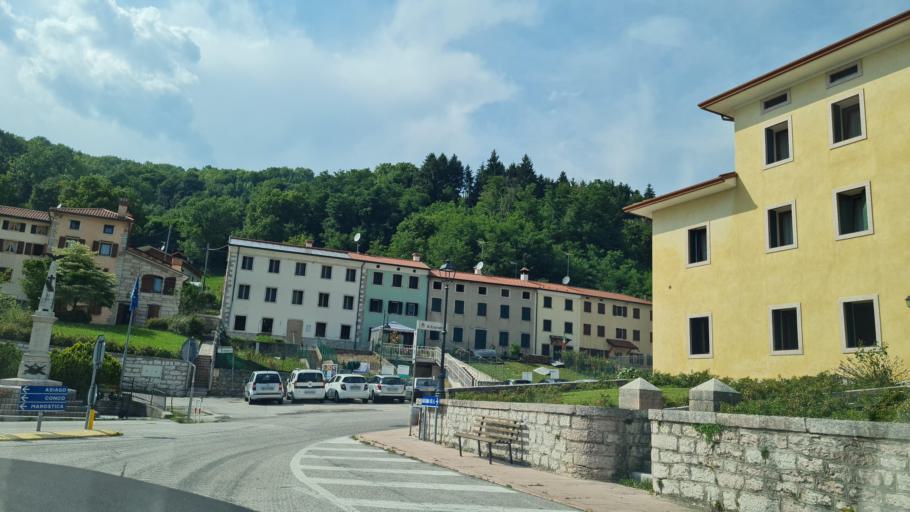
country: IT
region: Veneto
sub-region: Provincia di Vicenza
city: Conco
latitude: 45.7957
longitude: 11.6310
